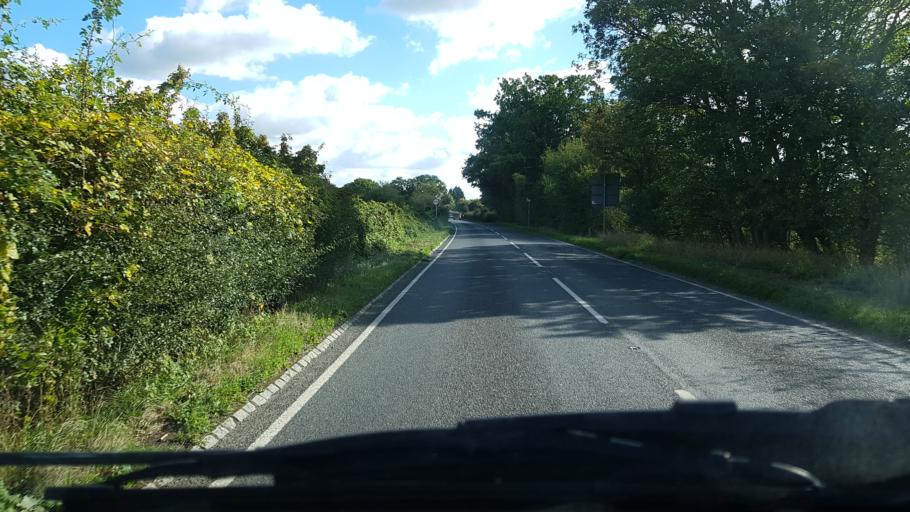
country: GB
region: England
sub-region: West Sussex
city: Billingshurst
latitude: 50.9974
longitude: -0.4661
